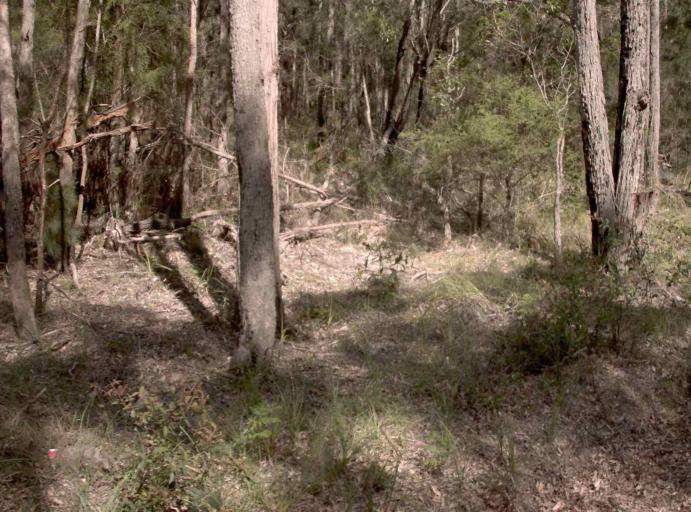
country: AU
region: New South Wales
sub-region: Bega Valley
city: Eden
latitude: -37.5343
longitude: 149.6963
